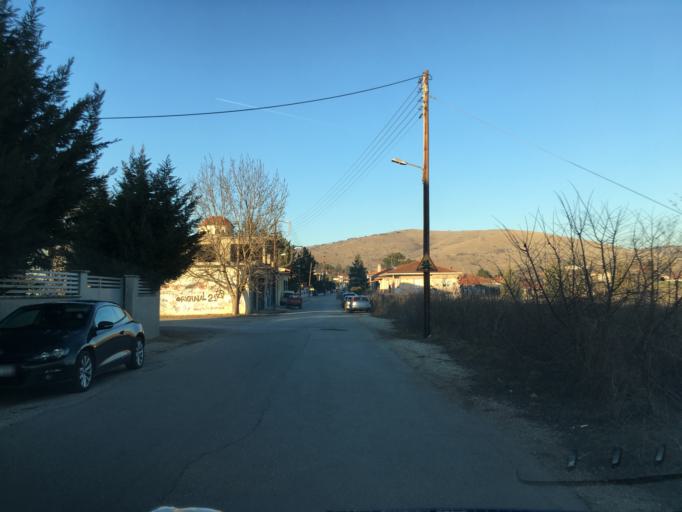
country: GR
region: West Macedonia
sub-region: Nomos Kozanis
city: Kozani
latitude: 40.2884
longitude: 21.7336
